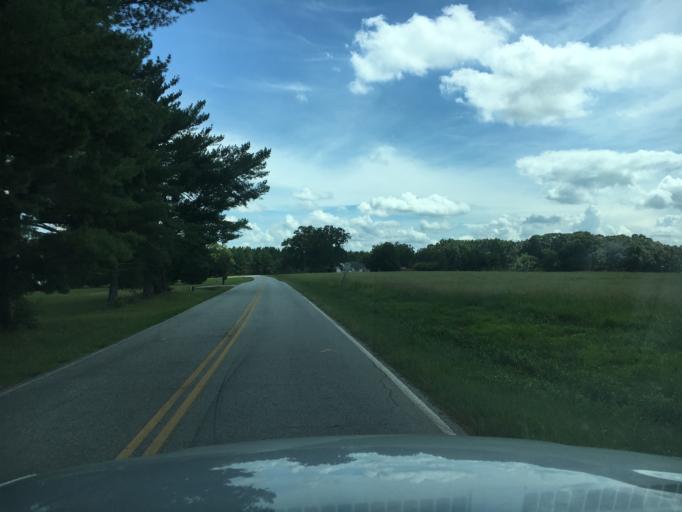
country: US
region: South Carolina
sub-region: Anderson County
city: Honea Path
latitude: 34.5031
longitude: -82.4093
